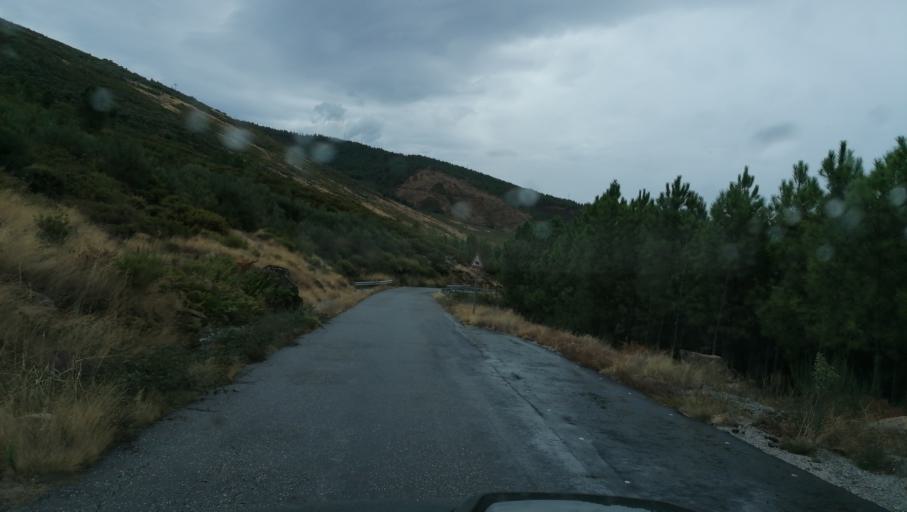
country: PT
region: Vila Real
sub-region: Vila Pouca de Aguiar
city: Vila Pouca de Aguiar
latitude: 41.5557
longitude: -7.7057
